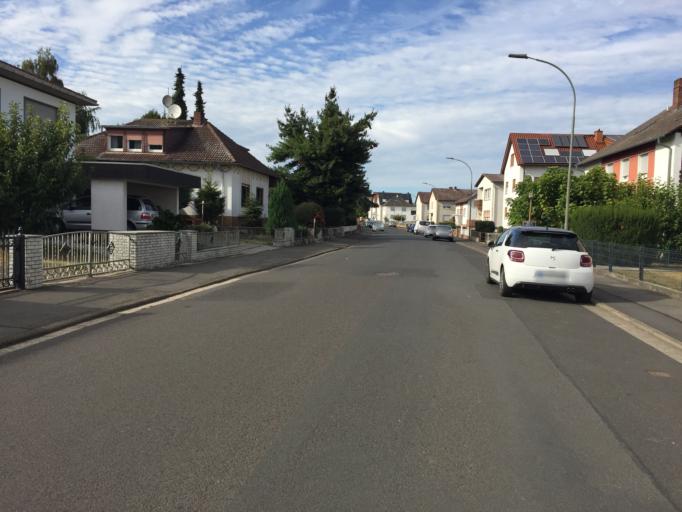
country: DE
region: Hesse
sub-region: Regierungsbezirk Darmstadt
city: Rockenberg
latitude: 50.4884
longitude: 8.7257
